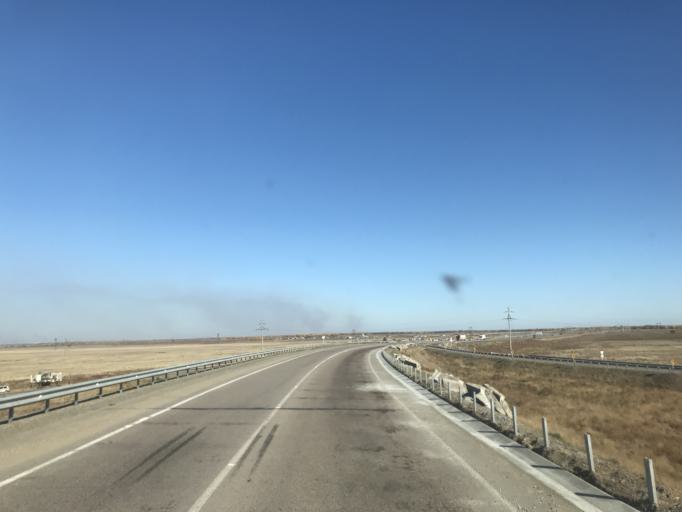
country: KZ
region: Pavlodar
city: Leninskiy
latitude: 52.1542
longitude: 76.8228
